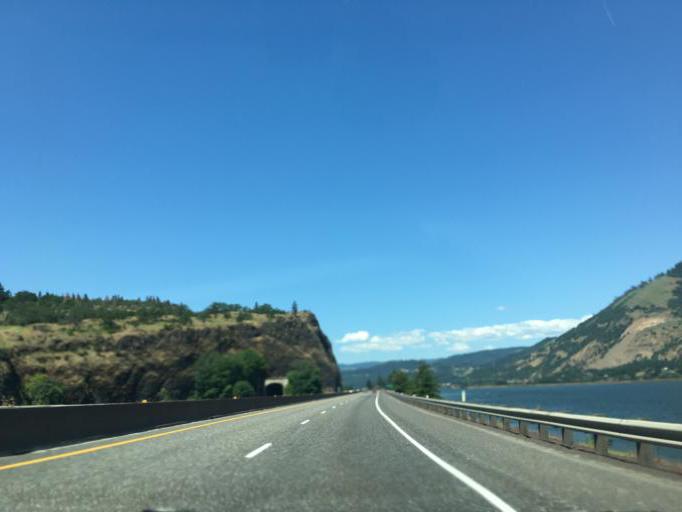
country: US
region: Washington
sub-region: Klickitat County
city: White Salmon
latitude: 45.6897
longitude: -121.4378
